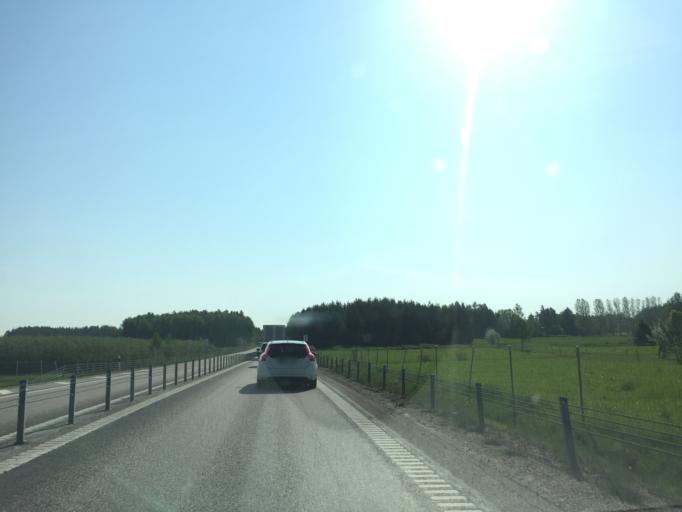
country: SE
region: Vaestmanland
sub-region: Hallstahammars Kommun
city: Kolback
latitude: 59.5791
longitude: 16.3281
